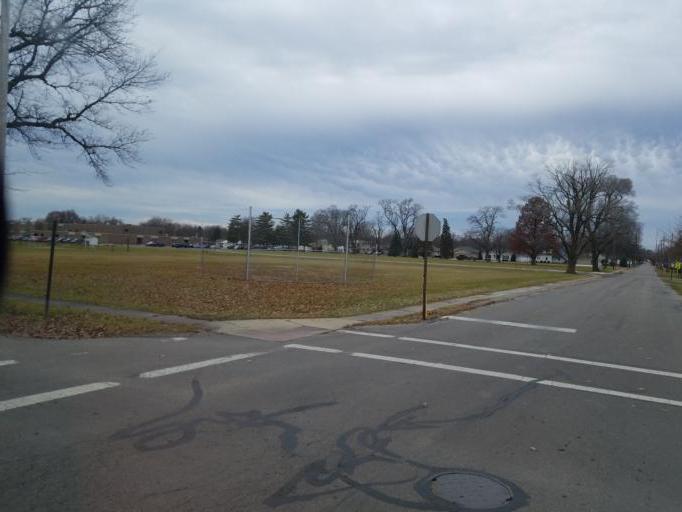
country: US
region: Ohio
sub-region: Marion County
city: Marion
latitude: 40.5855
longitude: -83.1024
